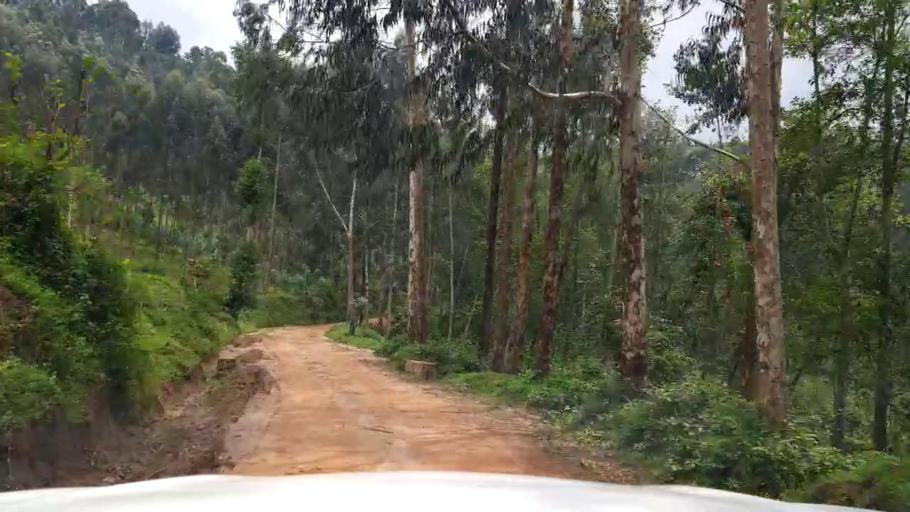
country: UG
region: Western Region
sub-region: Kabale District
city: Kabale
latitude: -1.4238
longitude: 29.8671
